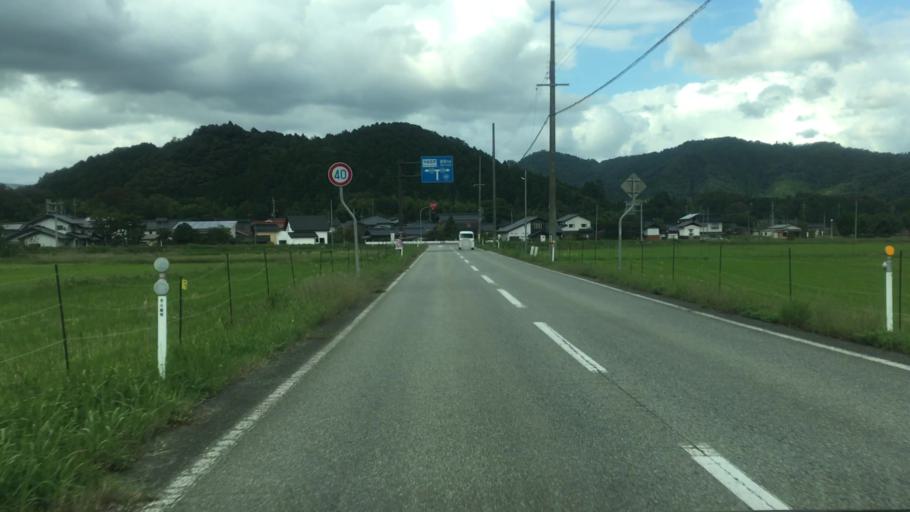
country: JP
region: Hyogo
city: Toyooka
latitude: 35.4519
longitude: 134.7291
